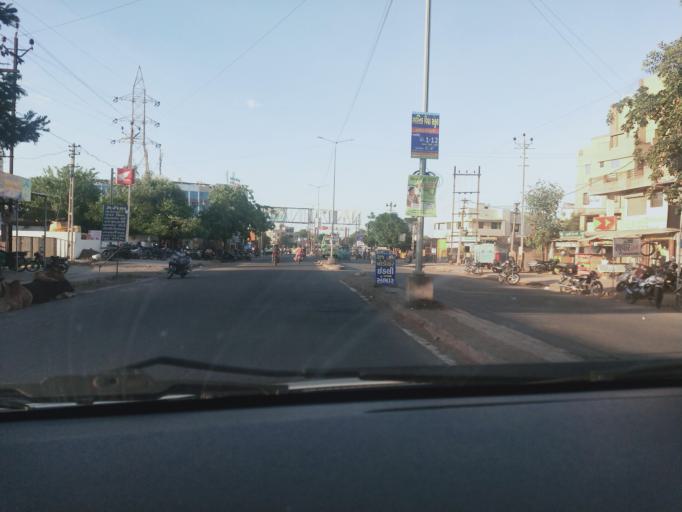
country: IN
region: Gujarat
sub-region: Bhavnagar
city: Bhavnagar
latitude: 21.6947
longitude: 72.1452
